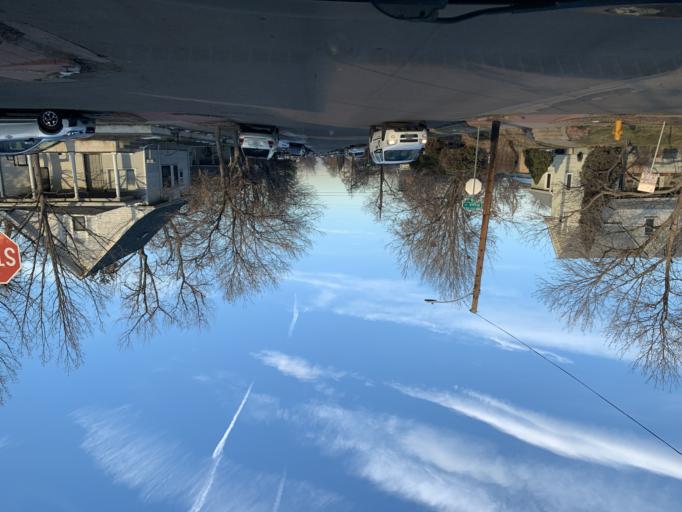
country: US
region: Colorado
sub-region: Adams County
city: Berkley
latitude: 39.7856
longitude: -105.0325
